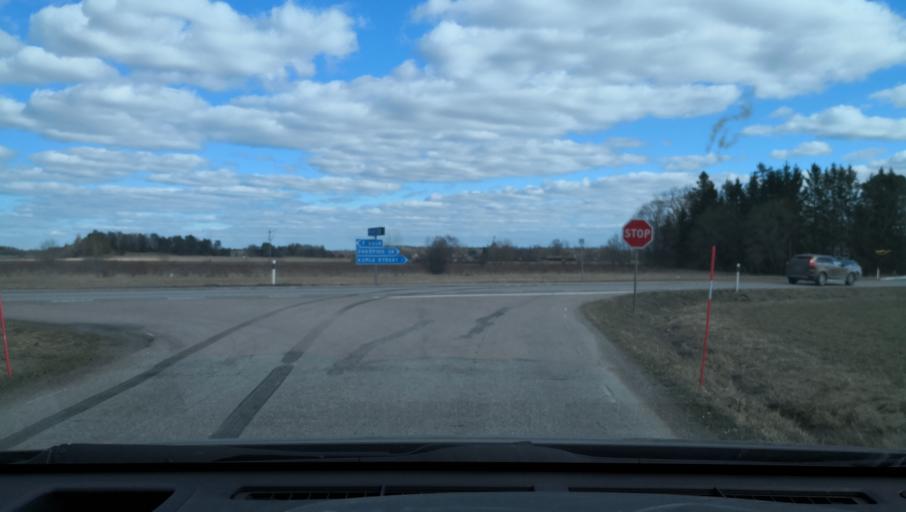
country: SE
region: Vaestmanland
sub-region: Sala Kommun
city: Sala
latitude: 59.8596
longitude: 16.6335
